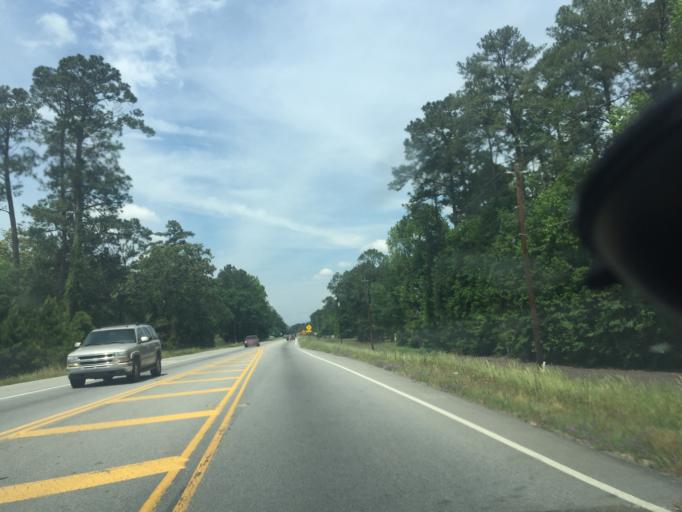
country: US
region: Georgia
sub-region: Chatham County
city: Bloomingdale
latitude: 32.1814
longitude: -81.3974
